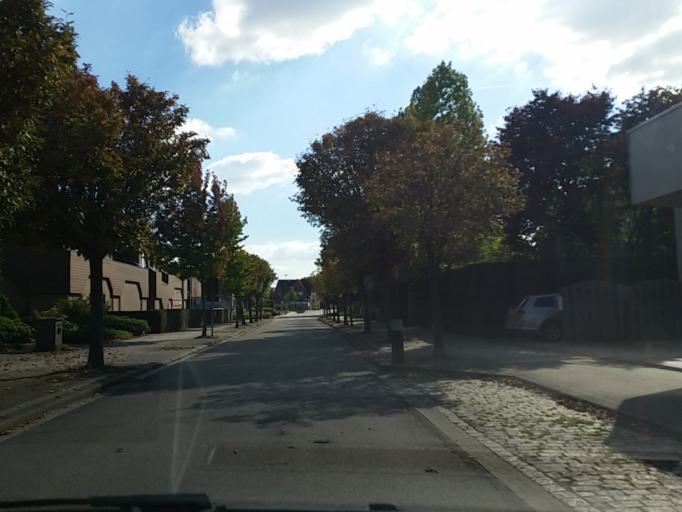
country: BE
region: Flanders
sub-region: Provincie Vlaams-Brabant
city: Rotselaar
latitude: 50.9314
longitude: 4.6972
